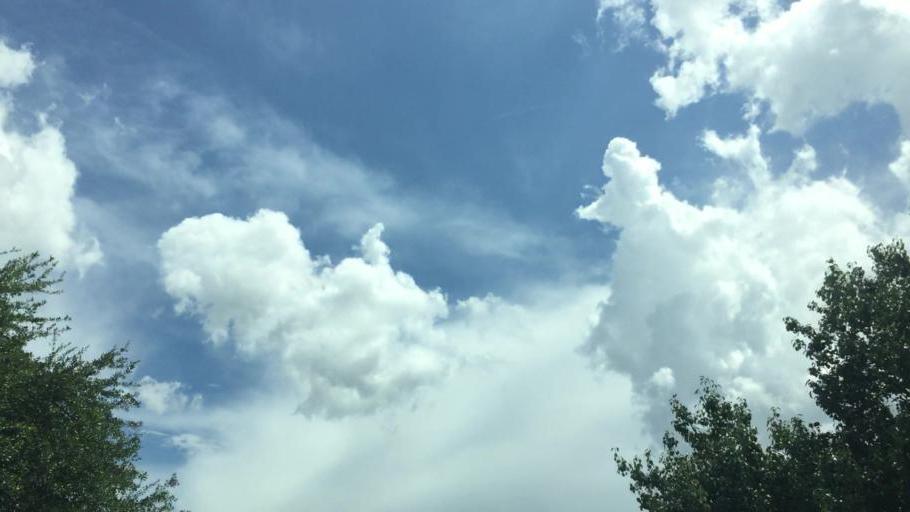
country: US
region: Texas
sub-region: Harris County
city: Bunker Hill Village
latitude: 29.7570
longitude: -95.5884
